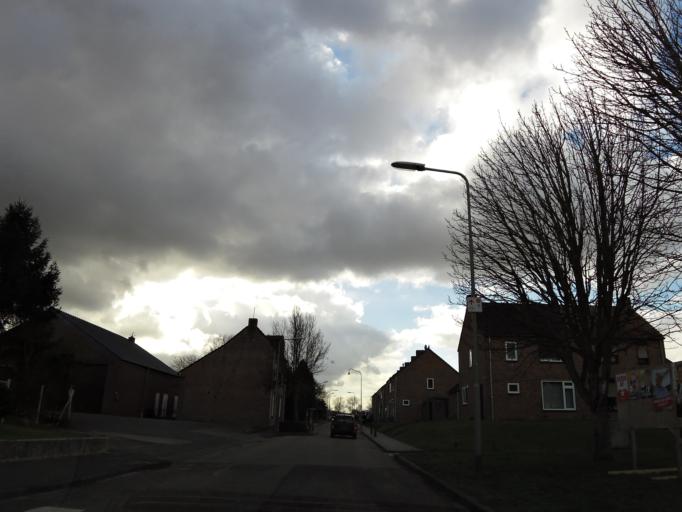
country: NL
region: Limburg
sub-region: Gemeente Onderbanken
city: Merkelbeek
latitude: 50.9790
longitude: 5.9383
